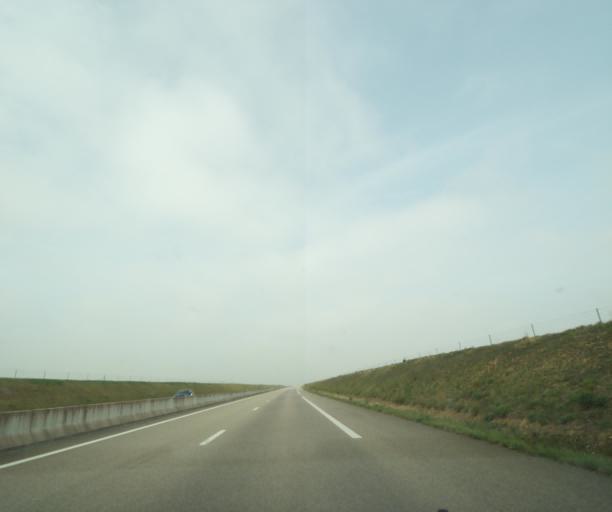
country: FR
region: Lower Normandy
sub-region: Departement de l'Orne
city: Argentan
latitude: 48.6952
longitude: -0.0243
